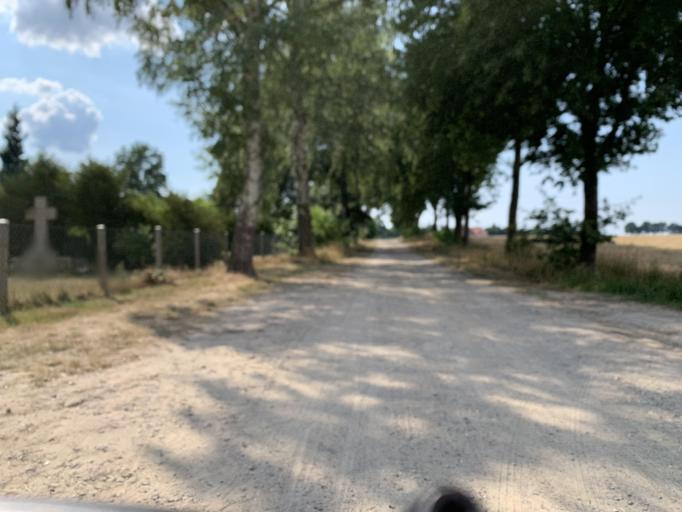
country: DE
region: Lower Saxony
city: Thomasburg
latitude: 53.2304
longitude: 10.6516
